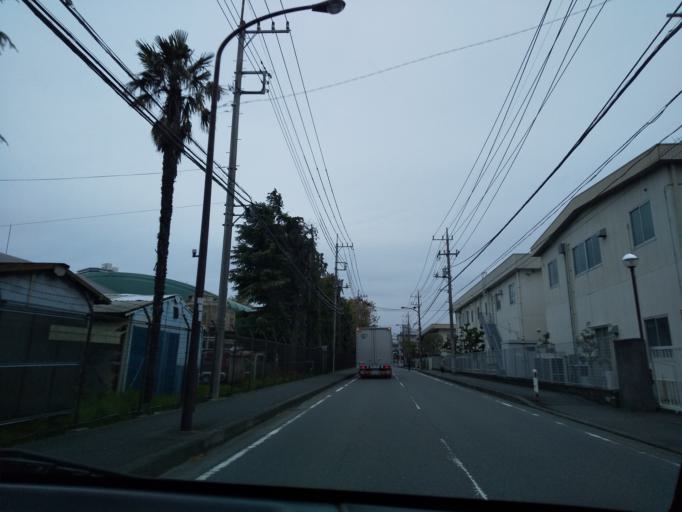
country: JP
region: Tokyo
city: Hachioji
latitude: 35.5910
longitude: 139.3589
